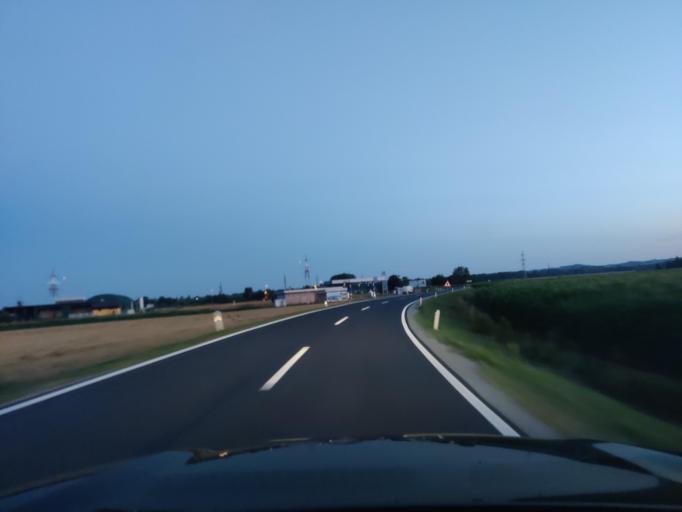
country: SI
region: Lendava-Lendva
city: Lendava
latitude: 46.5445
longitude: 16.4437
